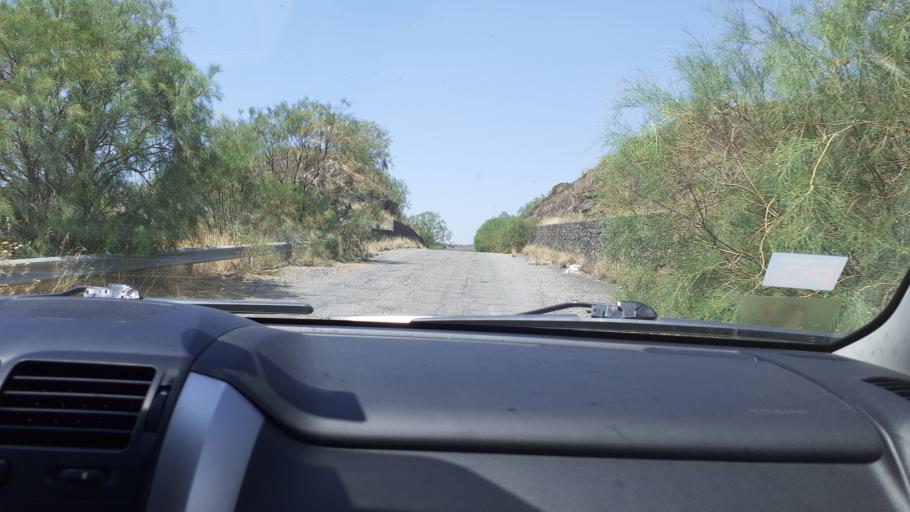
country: IT
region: Sicily
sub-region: Catania
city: Nicolosi
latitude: 37.6466
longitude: 15.0099
